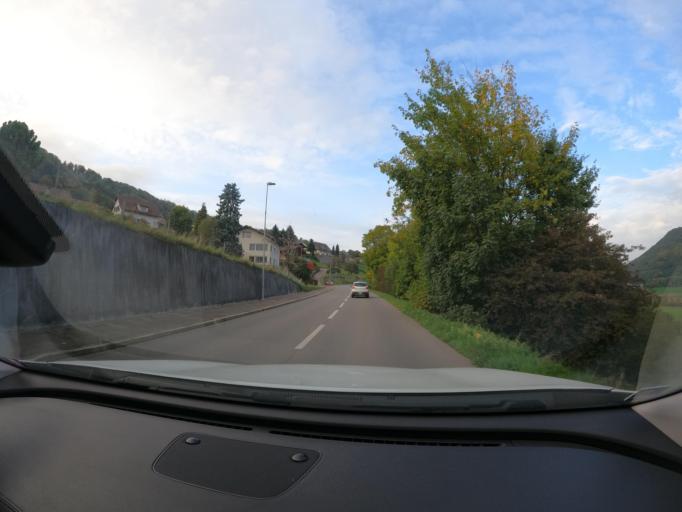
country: CH
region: Bern
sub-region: Bern-Mittelland District
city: Toffen
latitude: 46.8690
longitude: 7.4914
